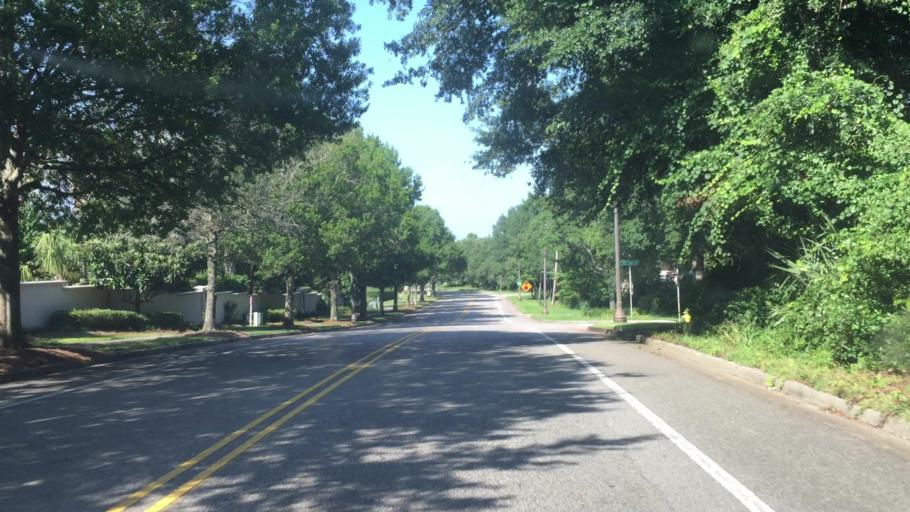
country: US
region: South Carolina
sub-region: Horry County
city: Myrtle Beach
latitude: 33.7480
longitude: -78.8119
